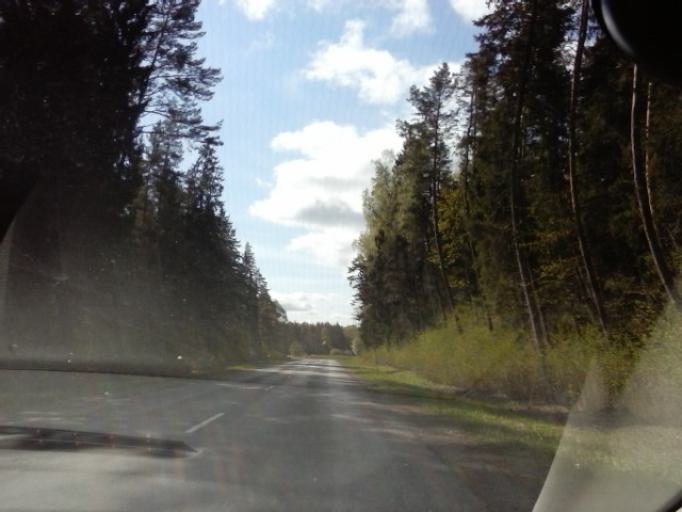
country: LV
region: Sigulda
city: Sigulda
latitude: 57.2203
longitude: 24.8558
